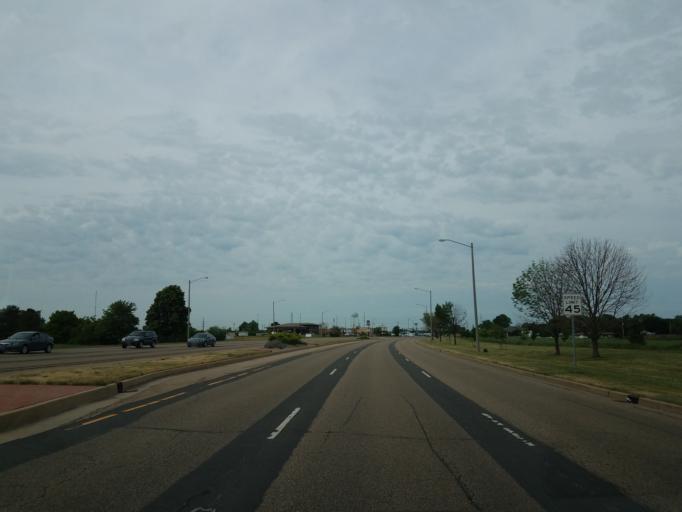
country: US
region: Illinois
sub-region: McLean County
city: Bloomington
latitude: 40.4634
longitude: -88.9582
